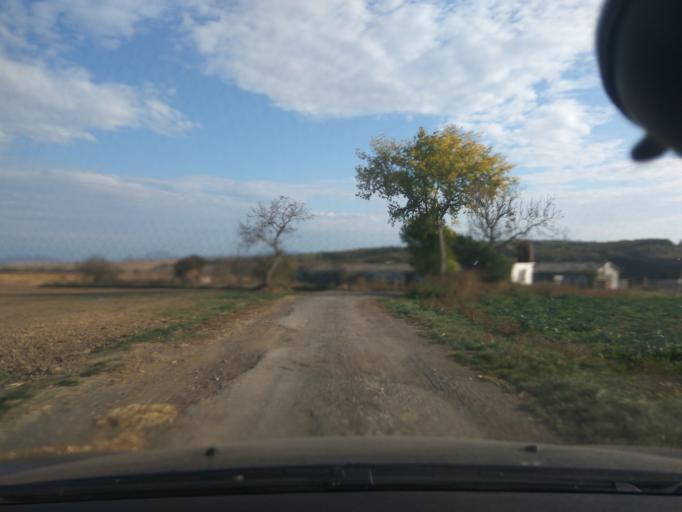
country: SK
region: Trnavsky
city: Hlohovec
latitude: 48.4463
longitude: 17.9254
